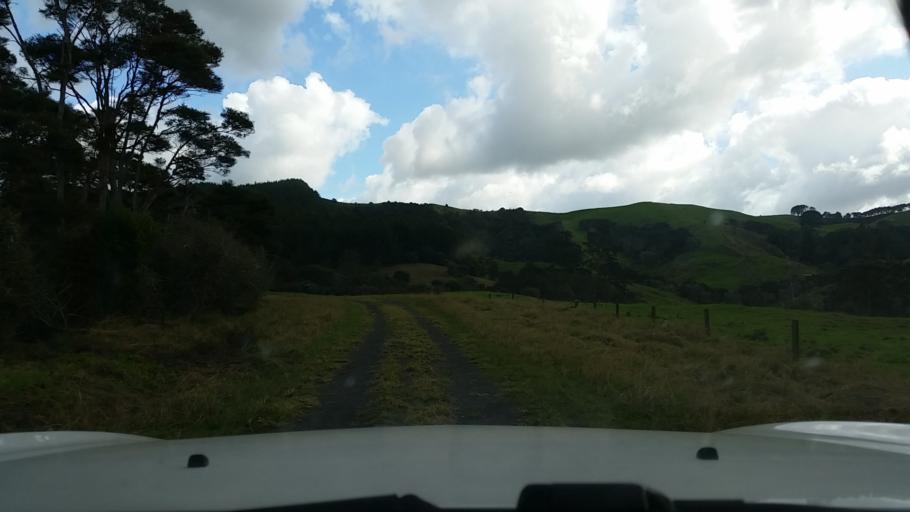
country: NZ
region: Waikato
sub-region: Hauraki District
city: Ngatea
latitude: -37.4372
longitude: 175.4734
